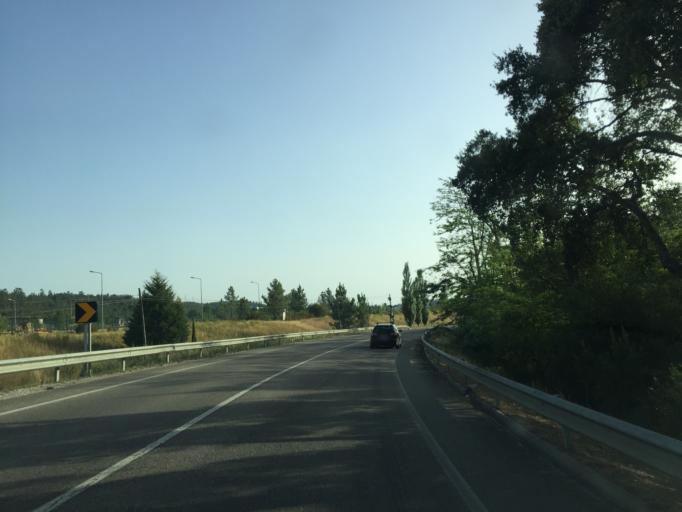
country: PT
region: Santarem
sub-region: Chamusca
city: Vila Nova da Barquinha
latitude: 39.5033
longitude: -8.4260
